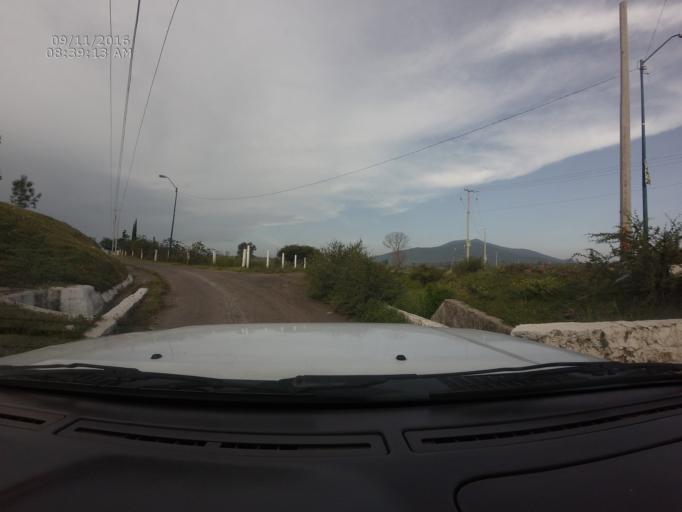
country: MX
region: Michoacan
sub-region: Morelia
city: La Mintzita (Piedra Dura)
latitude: 19.6200
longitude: -101.2814
